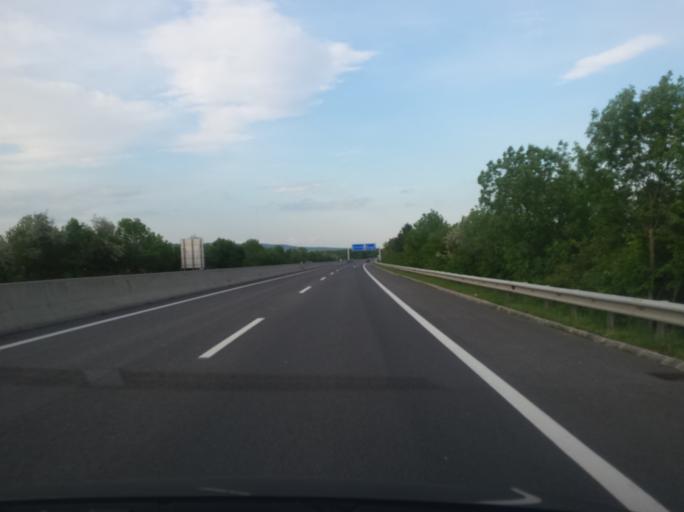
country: AT
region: Burgenland
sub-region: Eisenstadt-Umgebung
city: Wulkaprodersdorf
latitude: 47.8104
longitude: 16.4850
